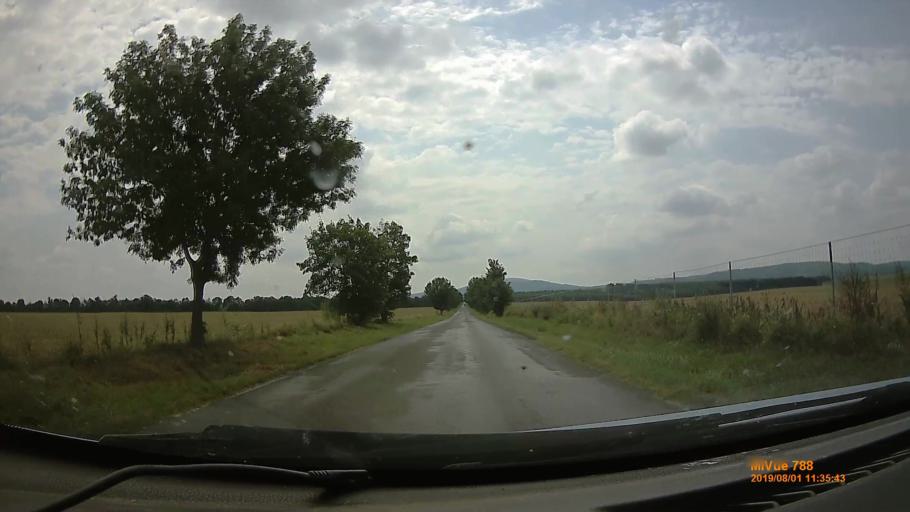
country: HU
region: Baranya
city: Siklos
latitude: 45.9246
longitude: 18.3700
